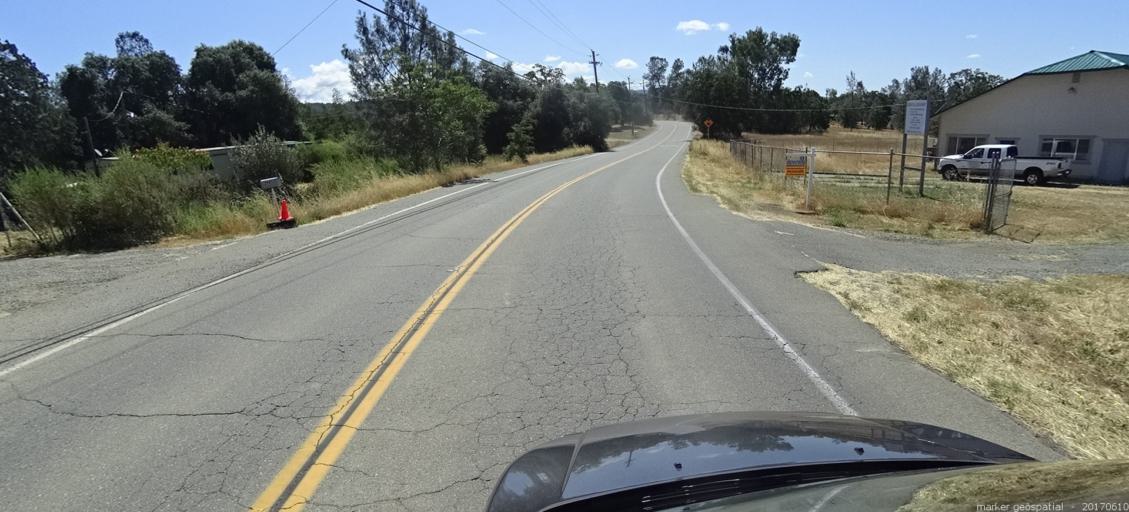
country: US
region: California
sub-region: Butte County
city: Oroville East
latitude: 39.5058
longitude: -121.5013
